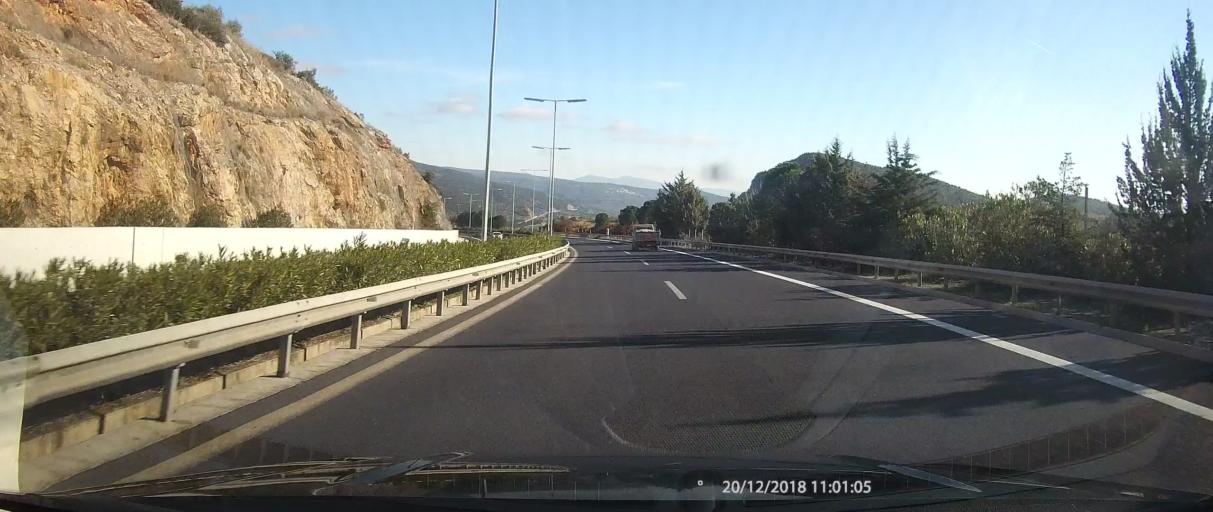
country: GR
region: Peloponnese
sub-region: Nomos Korinthias
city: Nemea
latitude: 37.7136
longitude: 22.5709
